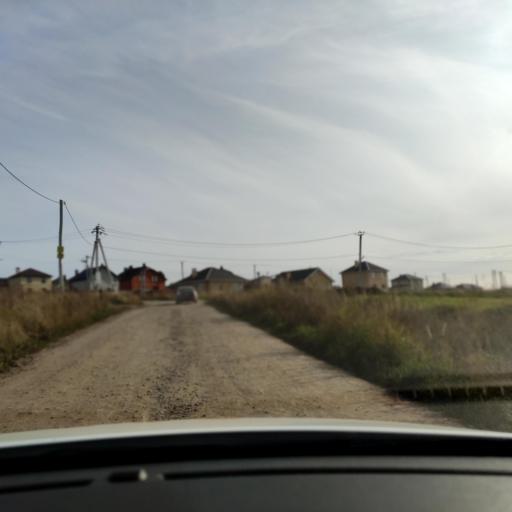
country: RU
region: Tatarstan
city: Vysokaya Gora
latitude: 55.8681
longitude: 49.3675
